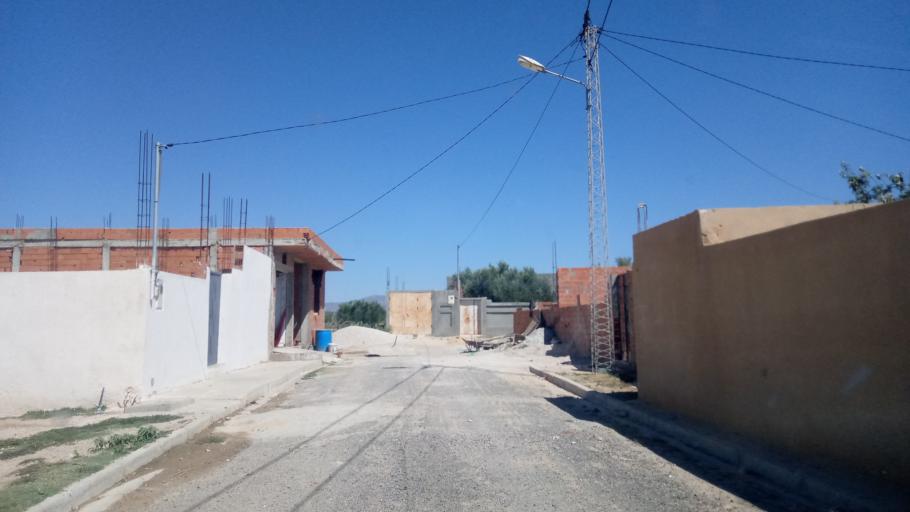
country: TN
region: Al Qayrawan
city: Sbikha
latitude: 36.1295
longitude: 10.0894
